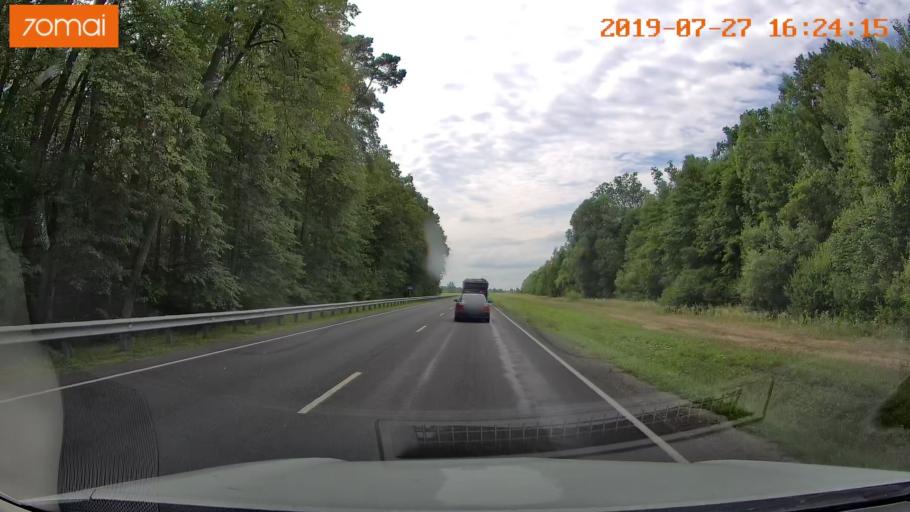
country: RU
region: Kaliningrad
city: Zheleznodorozhnyy
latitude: 54.6335
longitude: 21.4565
